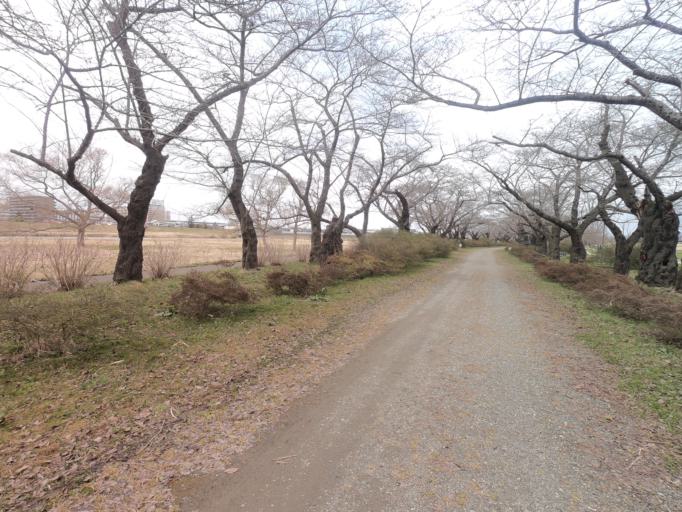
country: JP
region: Iwate
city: Kitakami
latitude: 39.2785
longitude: 141.1275
